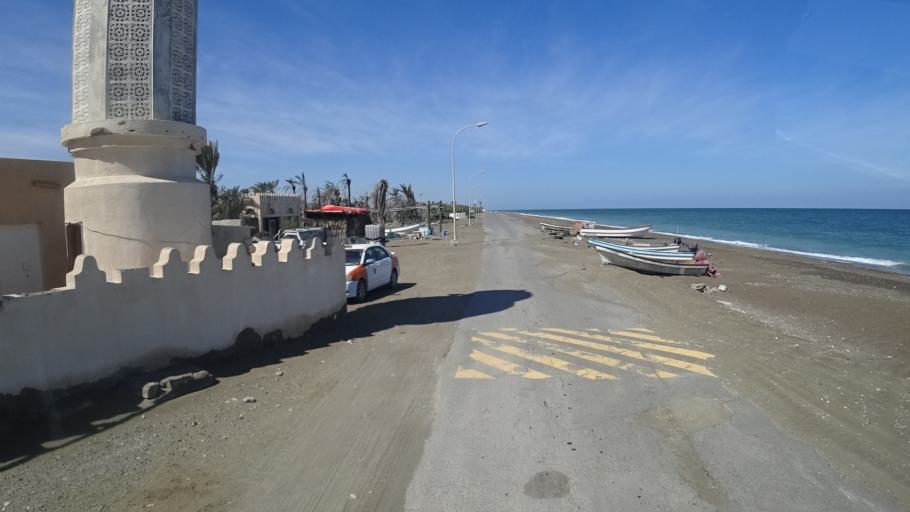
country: OM
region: Al Batinah
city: Al Sohar
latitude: 24.2728
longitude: 56.8151
